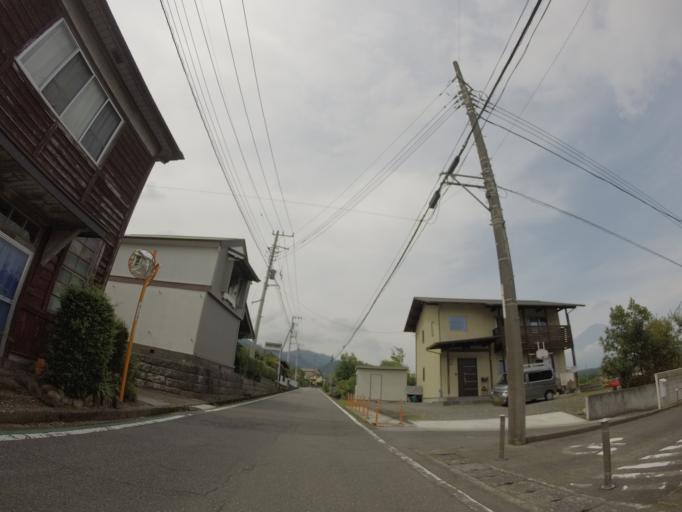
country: JP
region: Shizuoka
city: Fujinomiya
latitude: 35.2587
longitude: 138.5539
